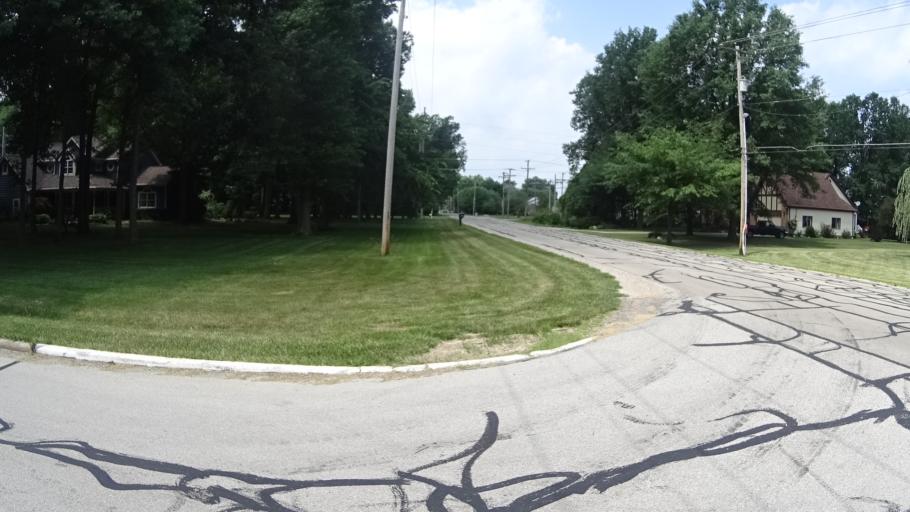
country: US
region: Ohio
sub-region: Lorain County
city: Vermilion
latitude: 41.4010
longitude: -82.3695
